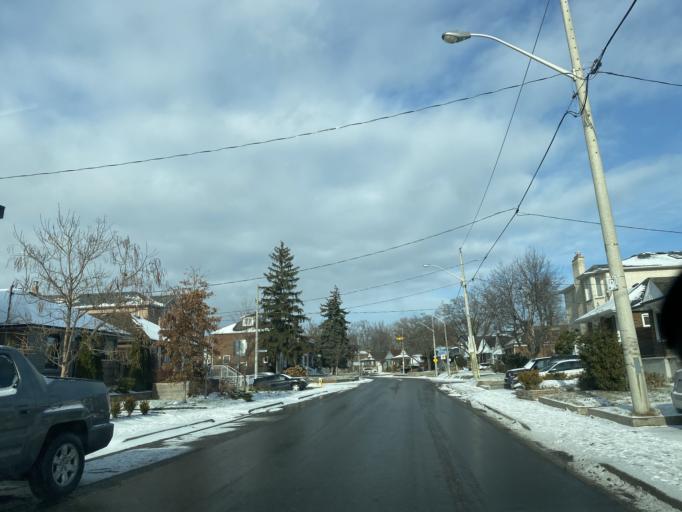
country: CA
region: Ontario
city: Toronto
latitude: 43.6899
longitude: -79.3359
